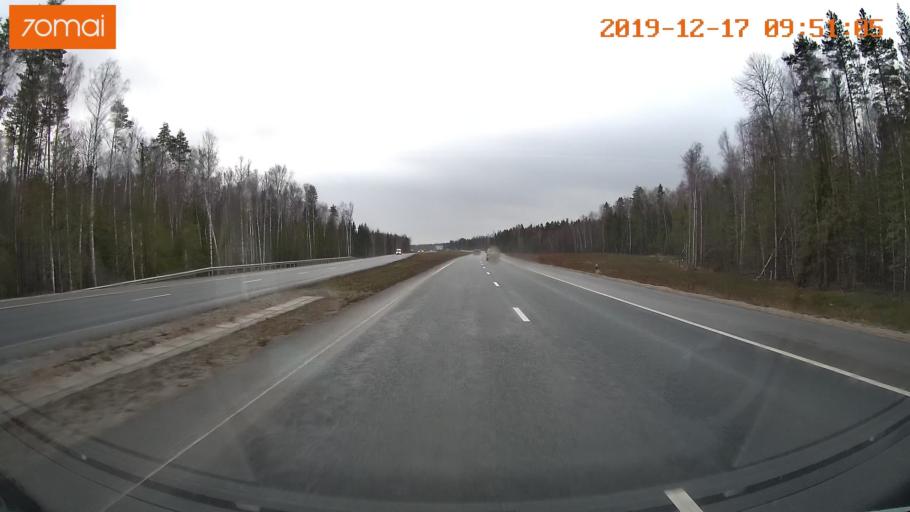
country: RU
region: Vladimir
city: Kommunar
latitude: 56.0491
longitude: 40.5169
